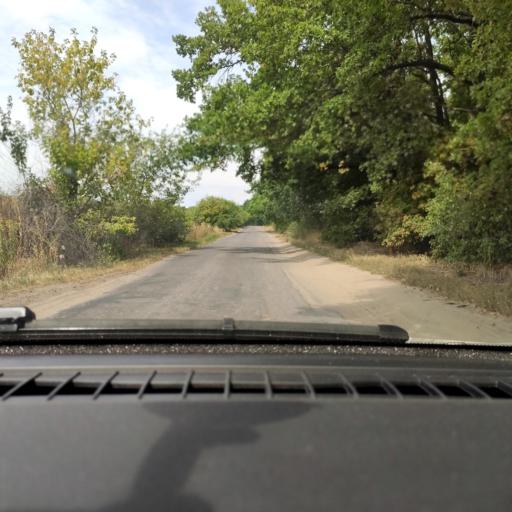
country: RU
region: Voronezj
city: Pridonskoy
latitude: 51.7354
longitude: 39.0609
